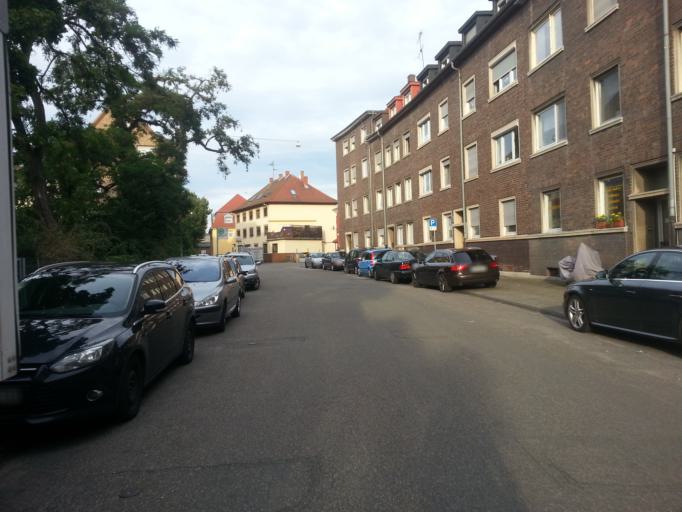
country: DE
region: Rheinland-Pfalz
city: Altrip
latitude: 49.4483
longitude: 8.4942
